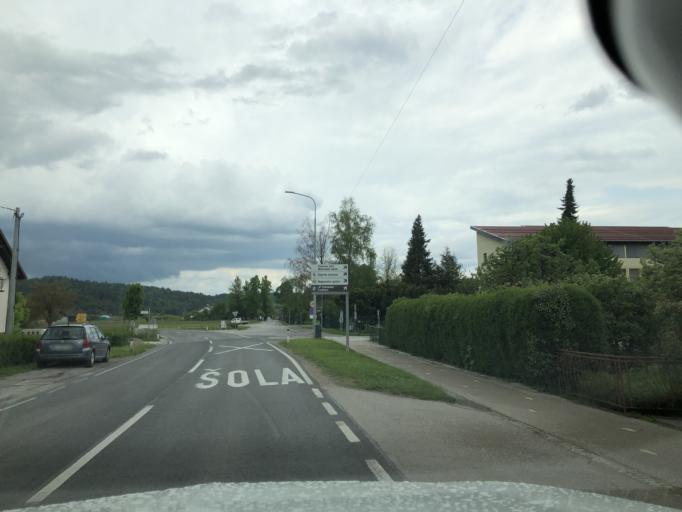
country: SI
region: Cerknica
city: Cerknica
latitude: 45.7956
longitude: 14.3574
